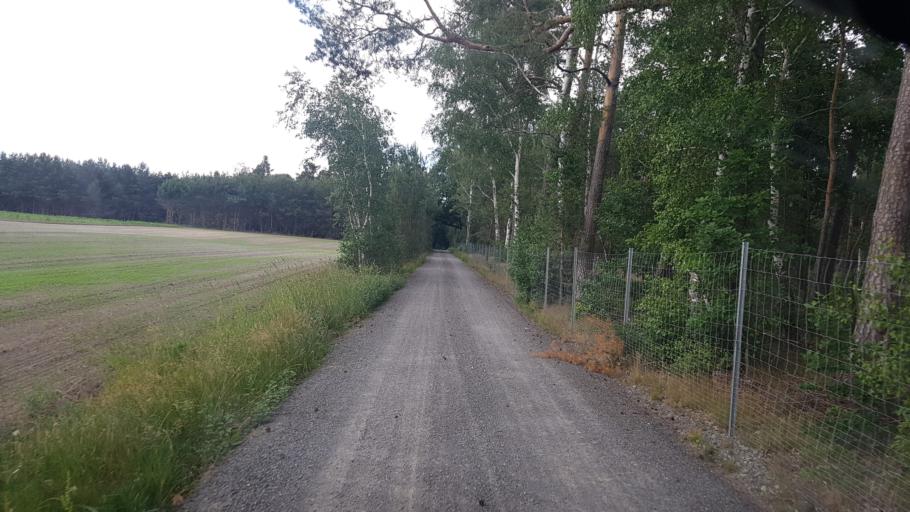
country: DE
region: Brandenburg
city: Plessa
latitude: 51.5426
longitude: 13.6401
